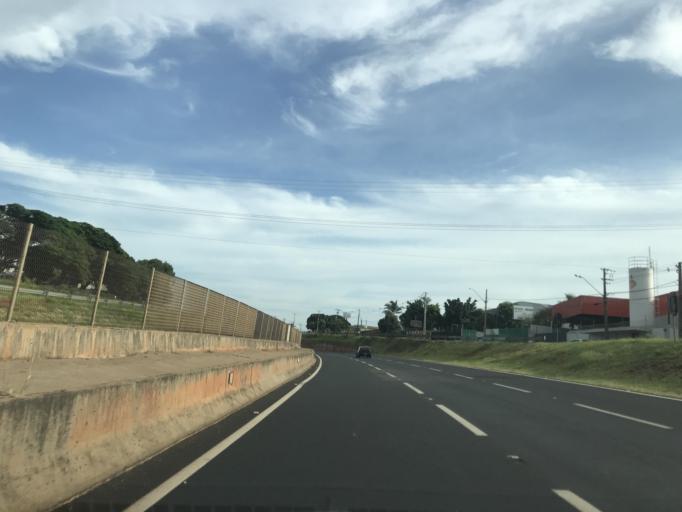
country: BR
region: Parana
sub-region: Mandaguacu
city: Mandaguacu
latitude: -23.3458
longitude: -52.0899
